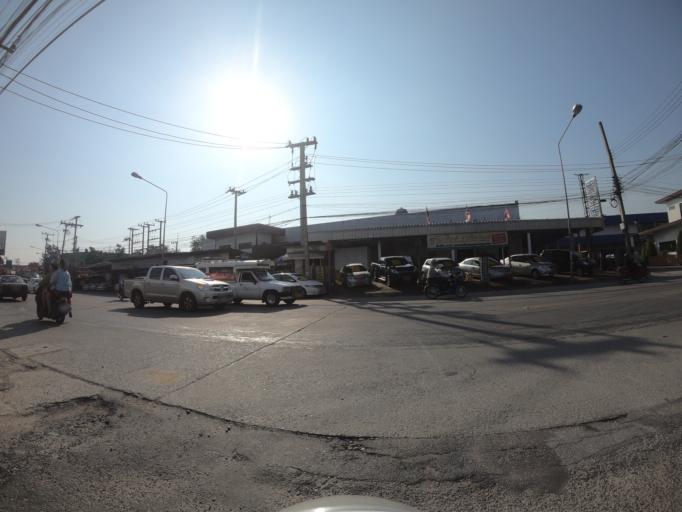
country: TH
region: Chiang Mai
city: Chiang Mai
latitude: 18.8001
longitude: 98.9932
